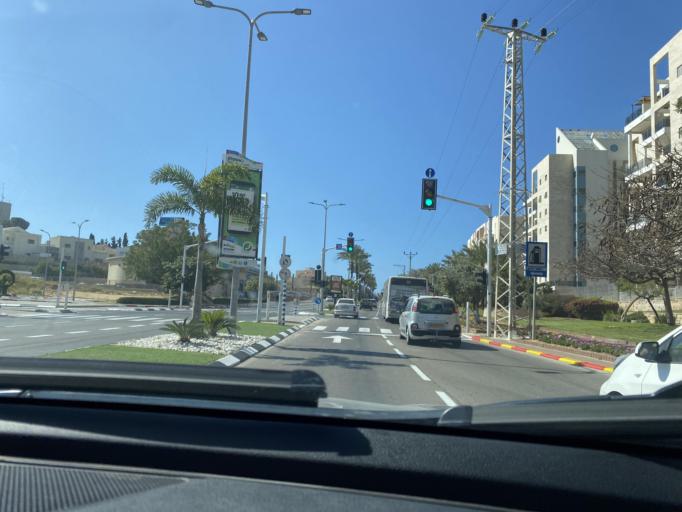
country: IL
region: Southern District
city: Ashqelon
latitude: 31.6767
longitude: 34.5767
